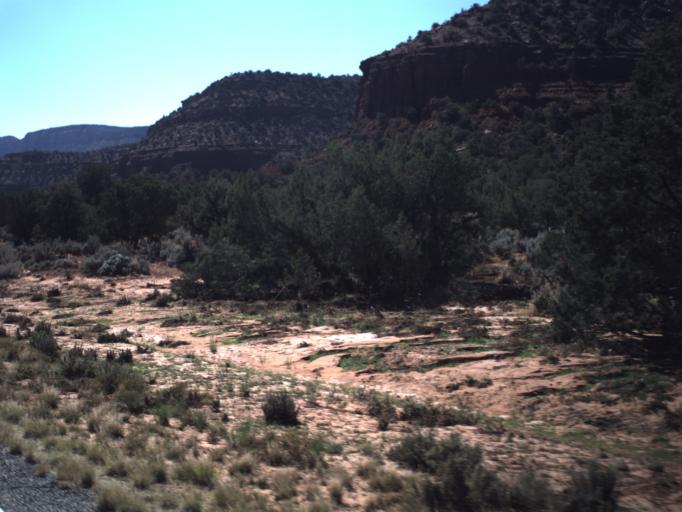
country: US
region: Utah
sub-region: San Juan County
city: Blanding
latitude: 37.6504
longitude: -110.1703
